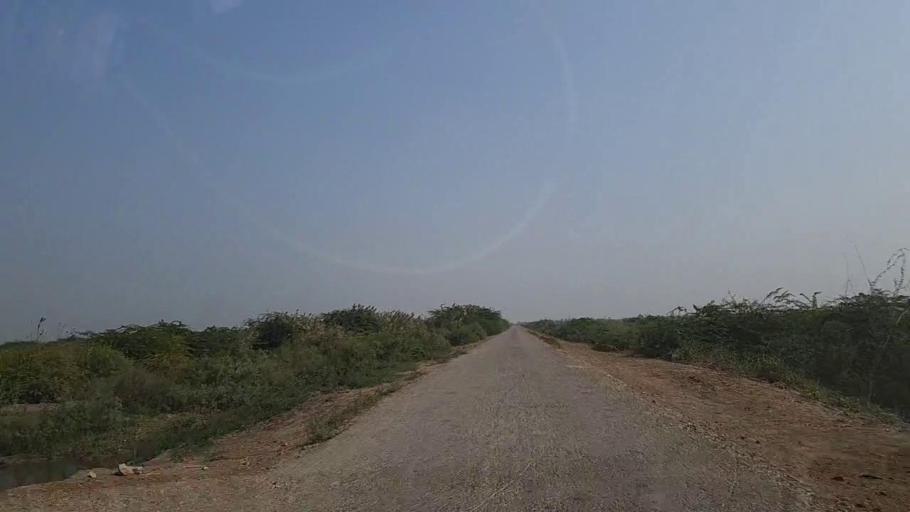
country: PK
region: Sindh
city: Keti Bandar
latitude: 24.2317
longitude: 67.6495
